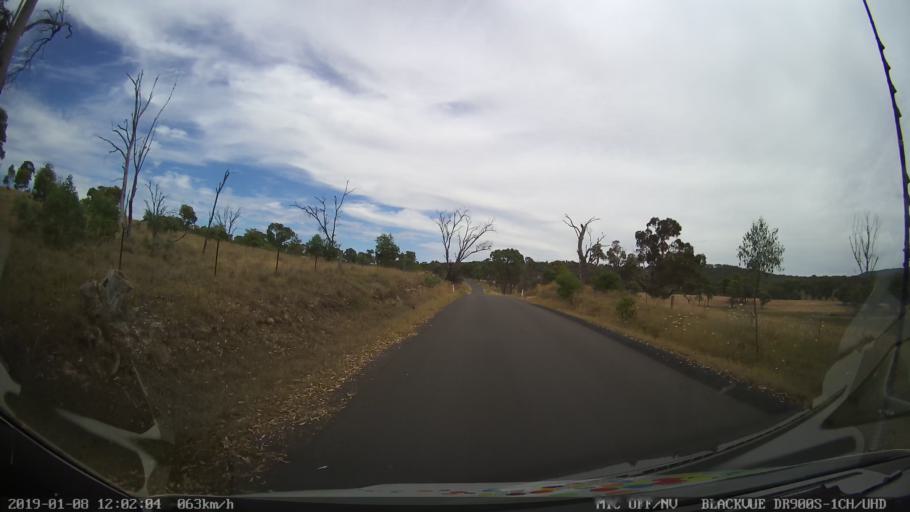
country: AU
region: New South Wales
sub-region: Armidale Dumaresq
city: Armidale
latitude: -30.4569
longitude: 151.6066
